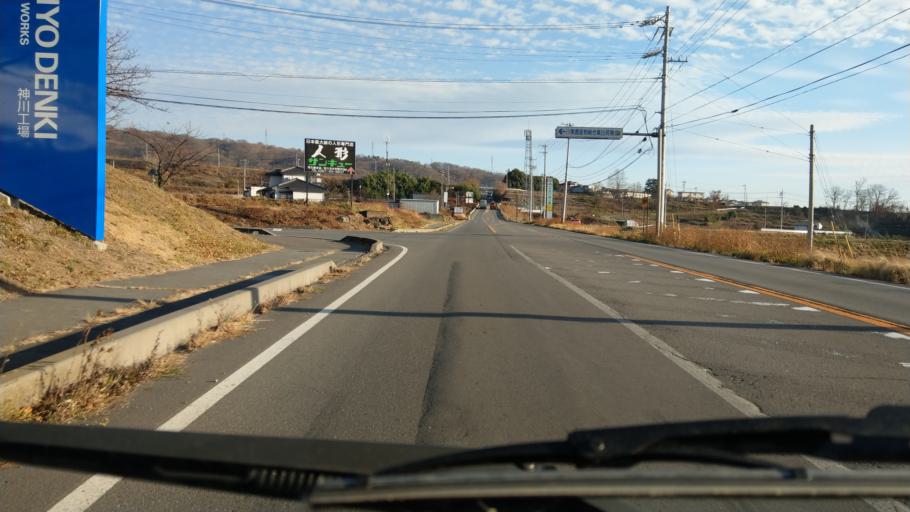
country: JP
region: Nagano
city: Ueda
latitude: 36.3963
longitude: 138.2968
